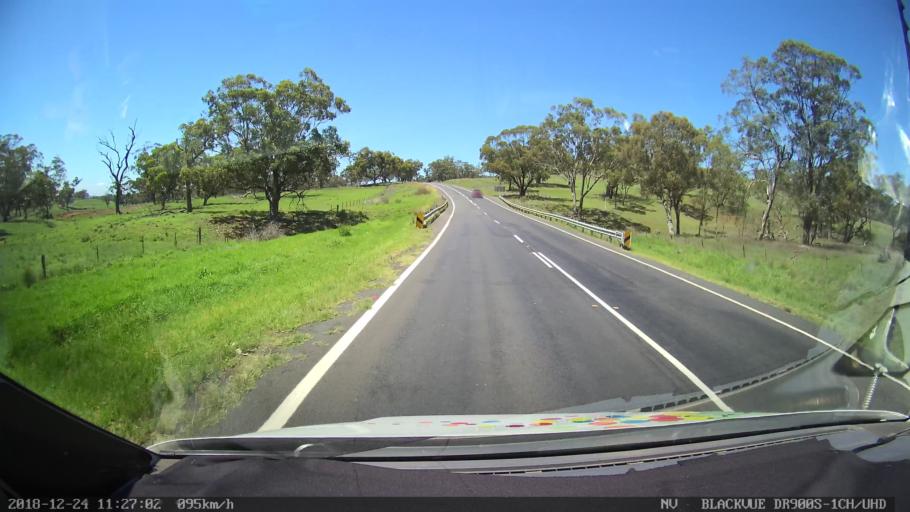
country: AU
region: New South Wales
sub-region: Upper Hunter Shire
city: Merriwa
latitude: -32.1769
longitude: 150.4339
